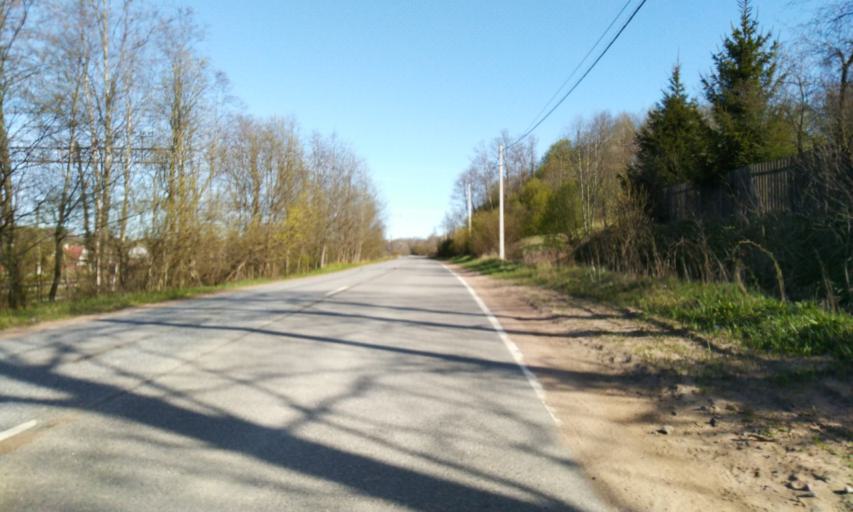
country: RU
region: Leningrad
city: Leskolovo
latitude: 60.3200
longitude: 30.4303
